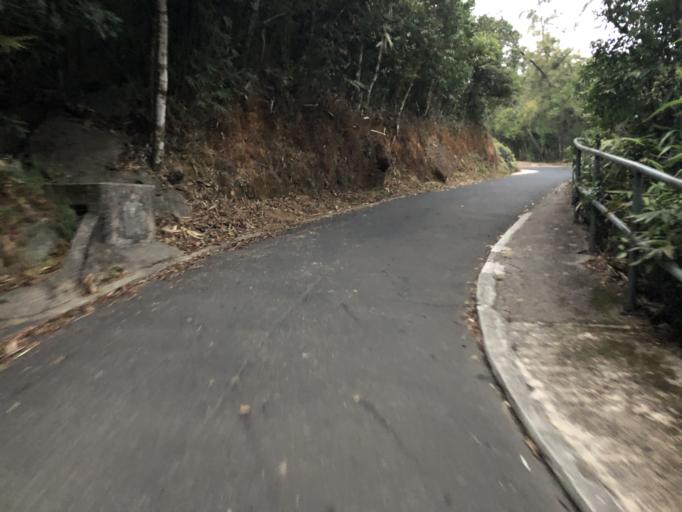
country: HK
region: Wanchai
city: Wan Chai
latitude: 22.2569
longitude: 114.2094
